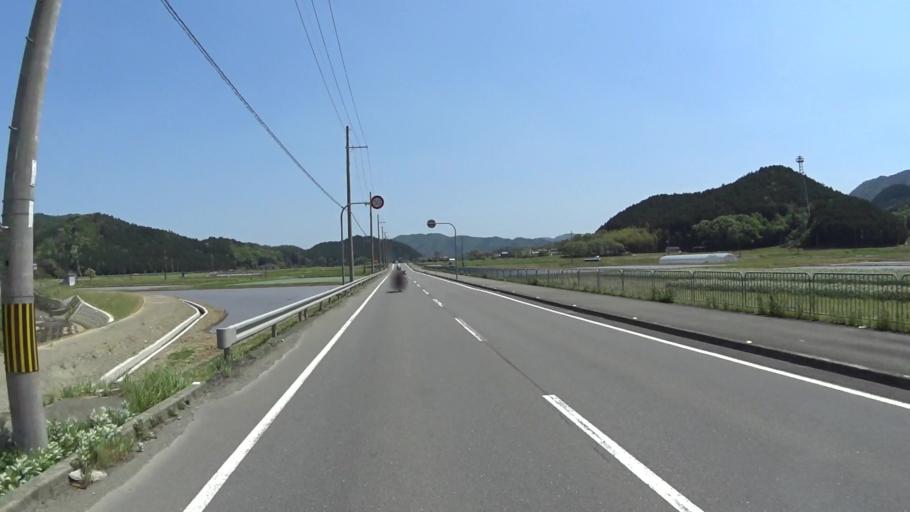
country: JP
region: Kyoto
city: Kameoka
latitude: 35.0477
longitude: 135.4778
